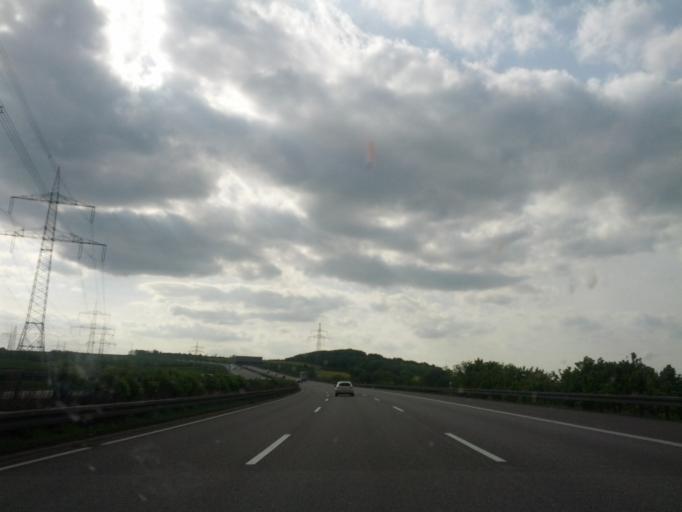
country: DE
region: Thuringia
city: Mellingen
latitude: 50.9351
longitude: 11.3831
